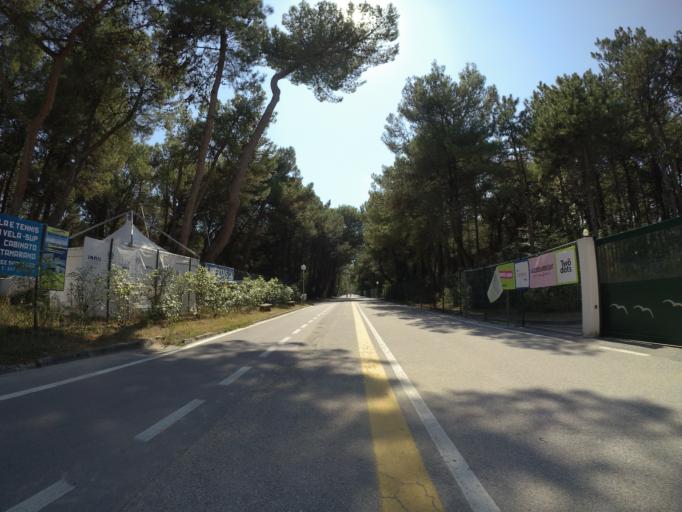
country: IT
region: Friuli Venezia Giulia
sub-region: Provincia di Udine
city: Lignano Sabbiadoro
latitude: 45.6766
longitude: 13.1245
